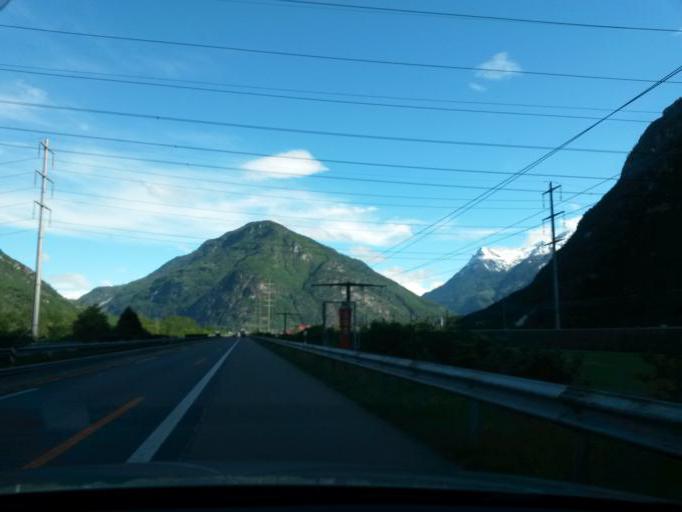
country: CH
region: Ticino
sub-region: Riviera District
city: Biasca
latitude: 46.3316
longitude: 8.9764
